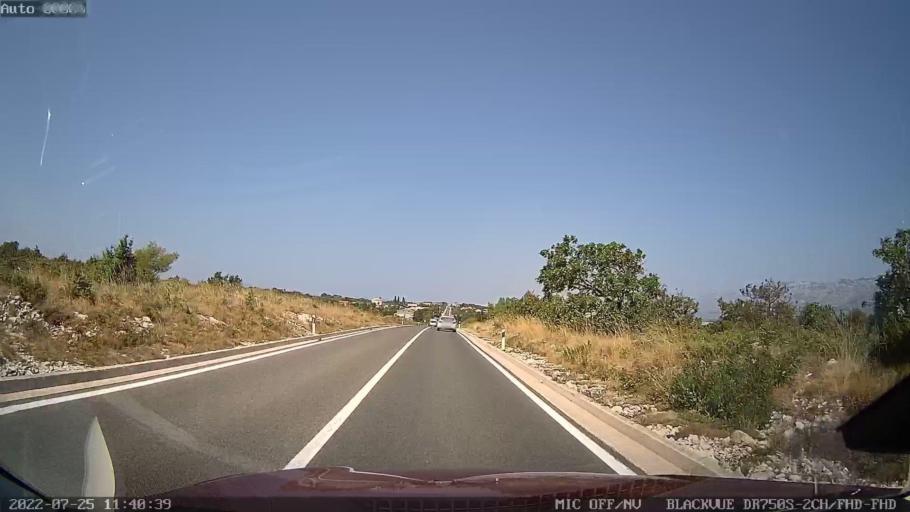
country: HR
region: Zadarska
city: Razanac
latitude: 44.2644
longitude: 15.3572
